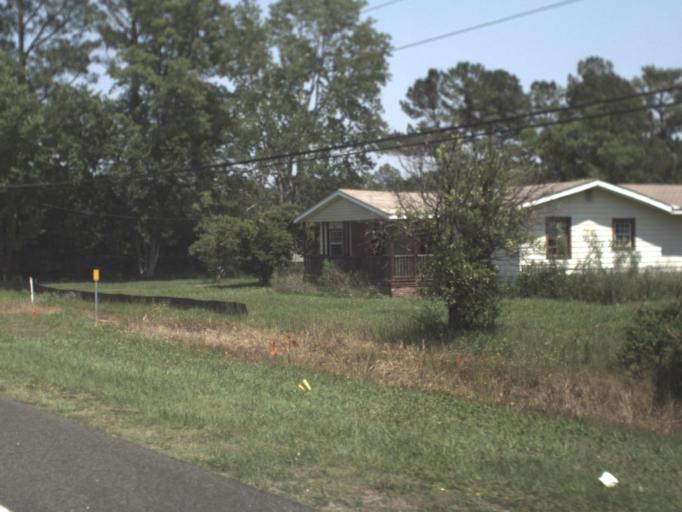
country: US
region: Florida
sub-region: Duval County
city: Baldwin
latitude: 30.2589
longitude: -81.8667
